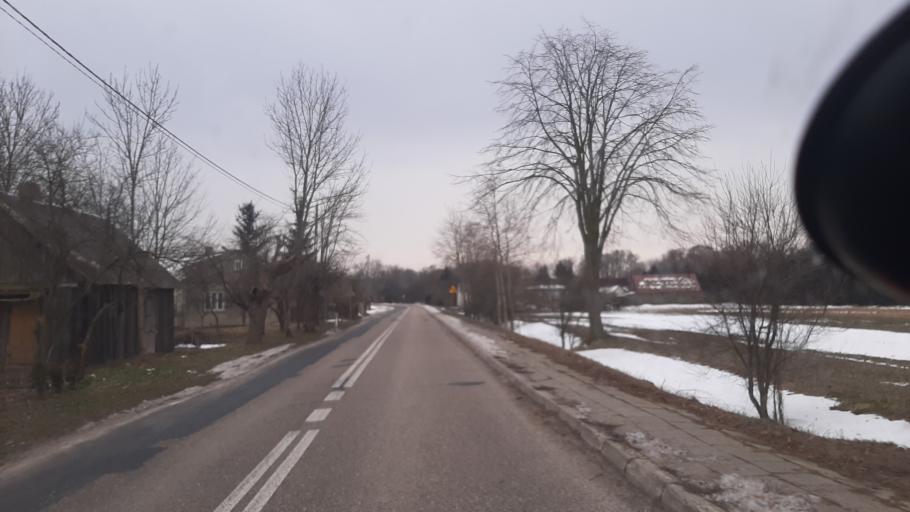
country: PL
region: Lublin Voivodeship
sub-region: Powiat lubartowski
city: Kamionka
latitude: 51.4502
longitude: 22.4215
